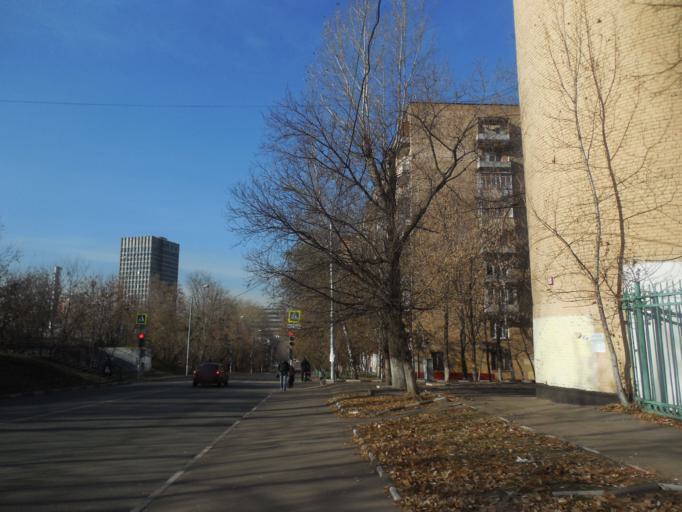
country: RU
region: Moscow
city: Lefortovo
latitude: 55.7762
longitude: 37.7067
